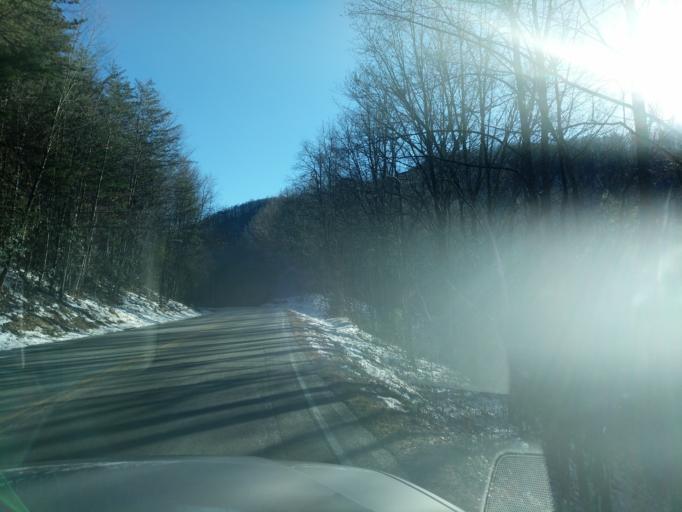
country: US
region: Georgia
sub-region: Towns County
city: Hiawassee
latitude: 34.9200
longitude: -83.6255
